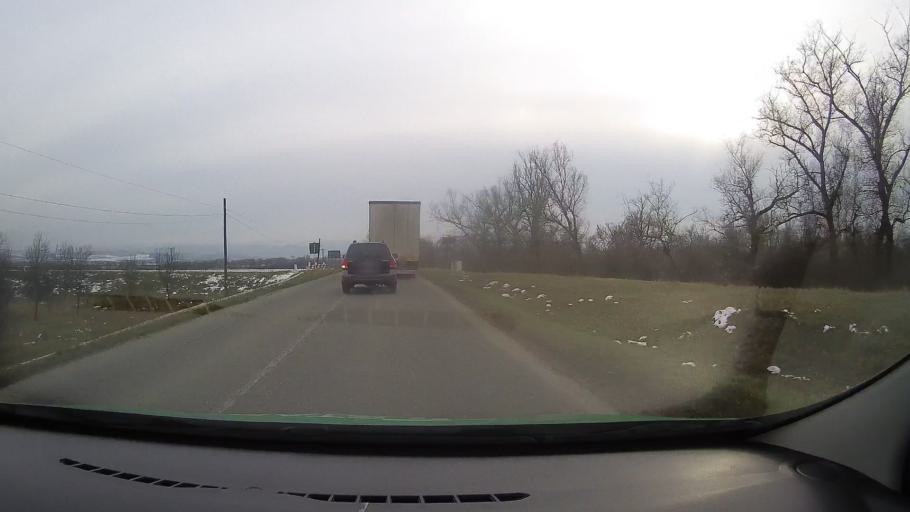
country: RO
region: Hunedoara
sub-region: Comuna Geoagiu
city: Geoagiu
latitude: 45.8992
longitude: 23.2250
